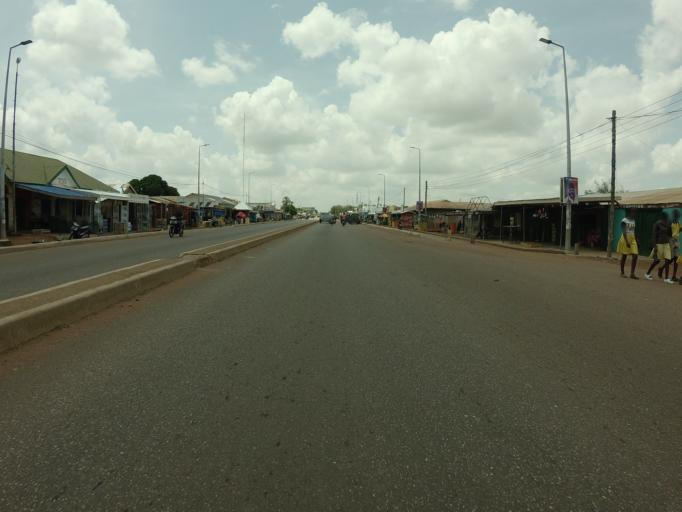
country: GH
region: Northern
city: Tamale
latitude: 9.3914
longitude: -0.8523
